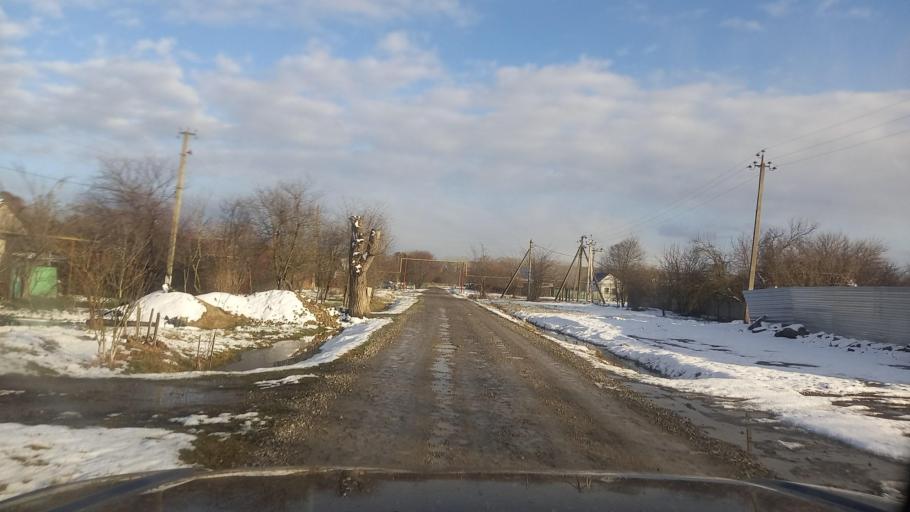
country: RU
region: Krasnodarskiy
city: Smolenskaya
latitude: 44.7762
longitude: 38.8475
